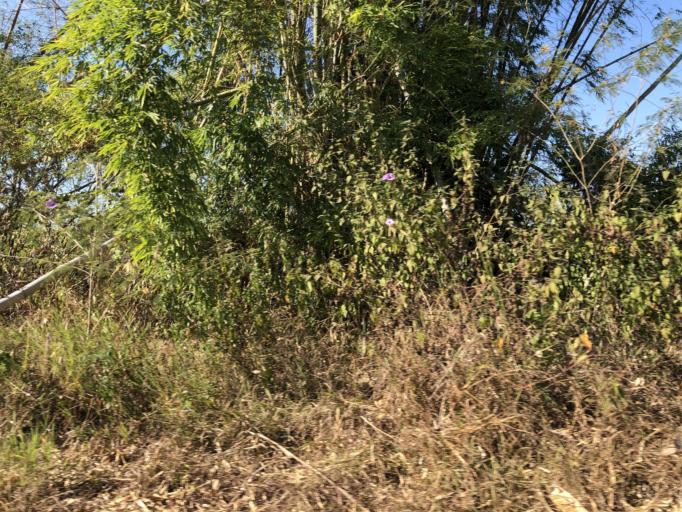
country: TW
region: Taiwan
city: Yujing
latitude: 23.0391
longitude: 120.3969
